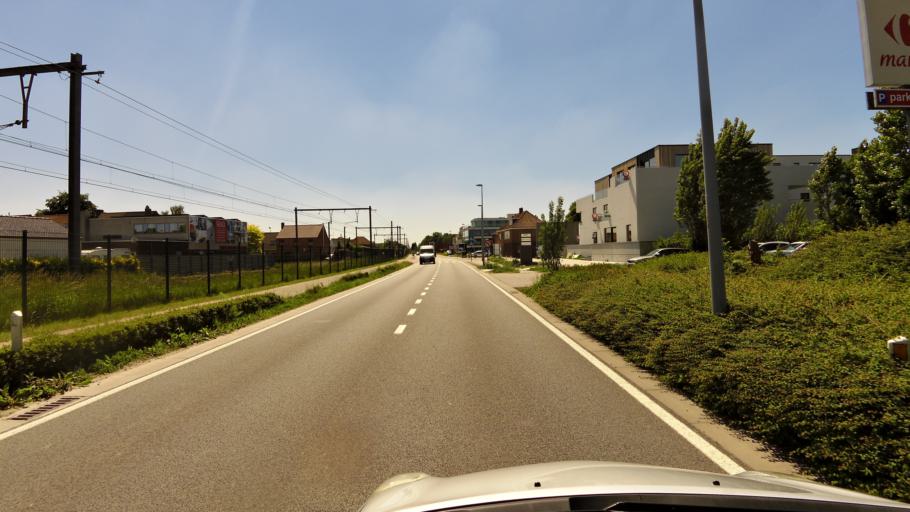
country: BE
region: Flanders
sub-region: Provincie West-Vlaanderen
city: Oostkamp
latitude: 51.1574
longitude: 3.1896
